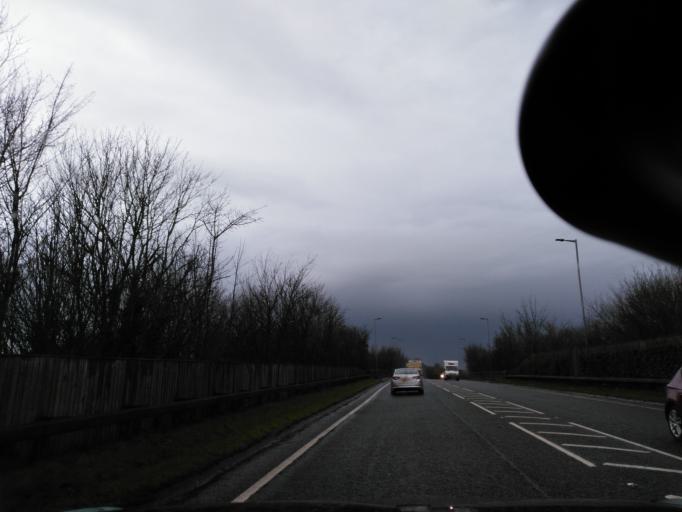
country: GB
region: England
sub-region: North Yorkshire
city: Ripon
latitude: 54.1325
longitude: -1.5122
